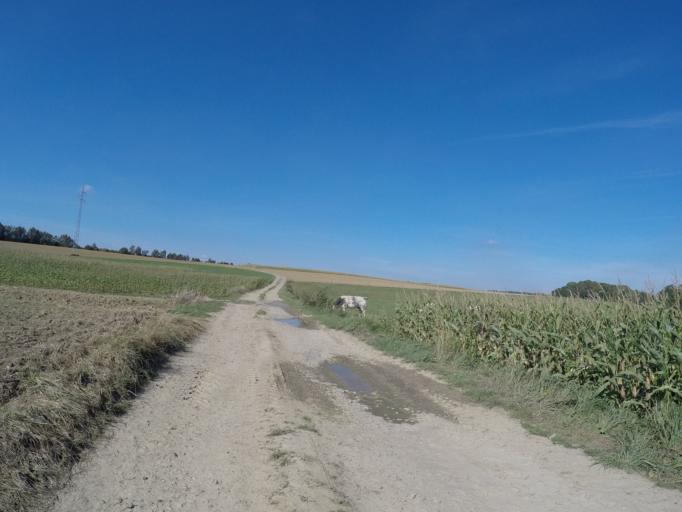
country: BE
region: Wallonia
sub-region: Province de Namur
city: Assesse
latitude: 50.3046
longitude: 5.0237
